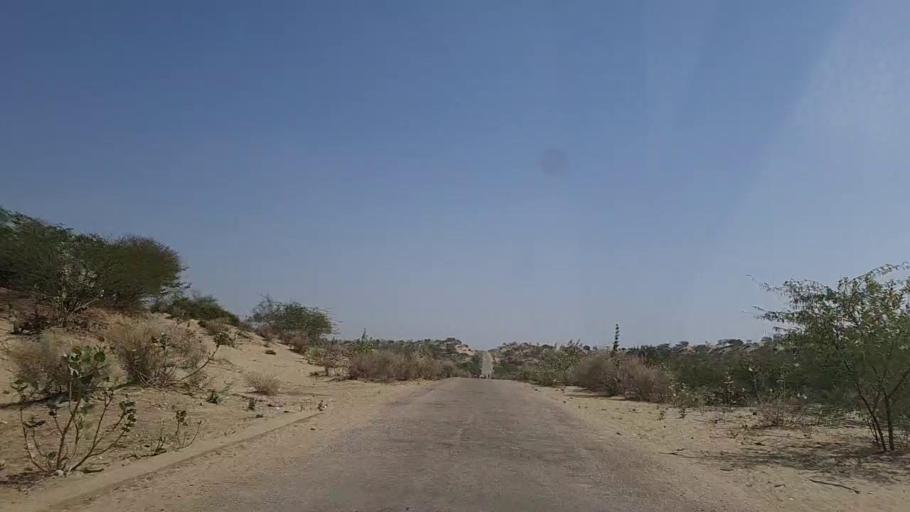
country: PK
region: Sindh
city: Diplo
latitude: 24.5136
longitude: 69.4025
